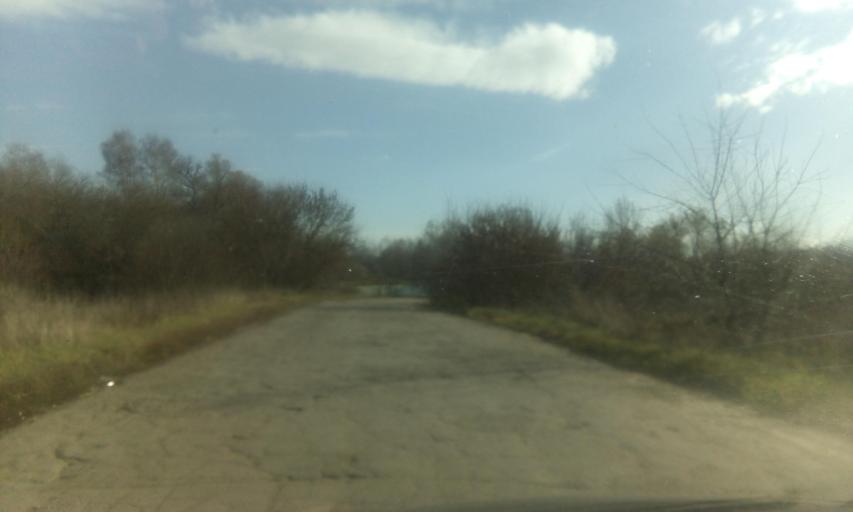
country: RU
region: Tula
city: Dubovka
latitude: 53.9488
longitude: 38.0282
